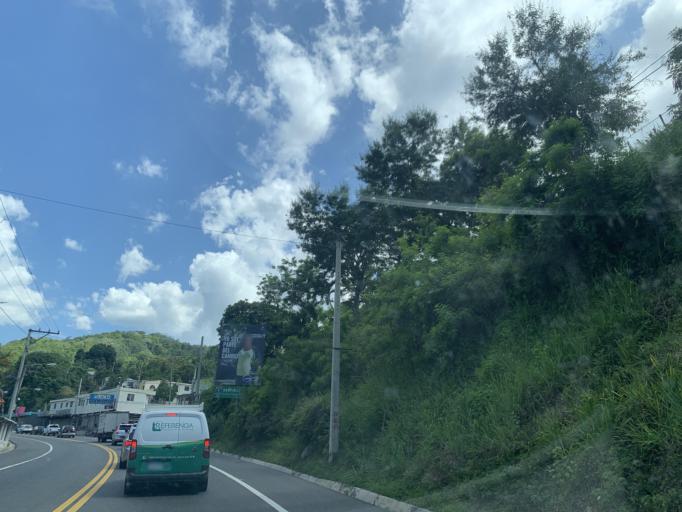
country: DO
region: Puerto Plata
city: Altamira
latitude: 19.6742
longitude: -70.8354
